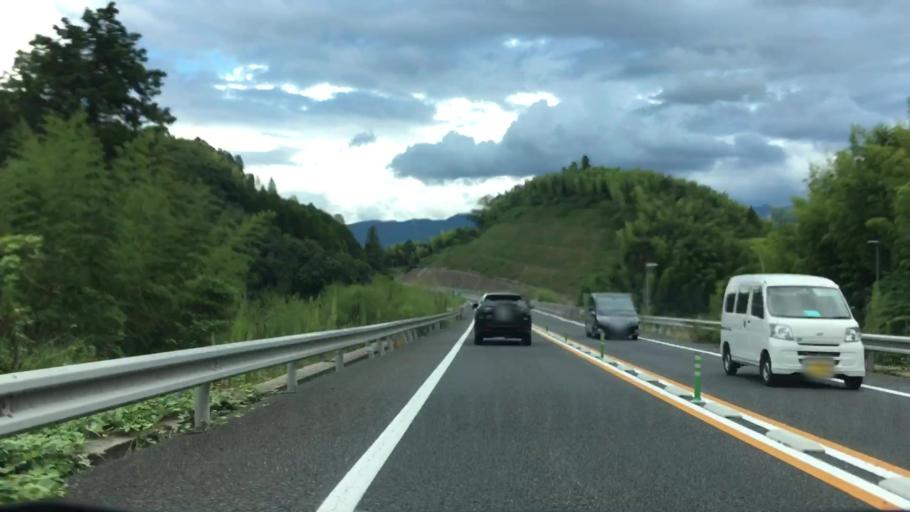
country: JP
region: Saga Prefecture
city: Karatsu
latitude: 33.4032
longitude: 129.9525
